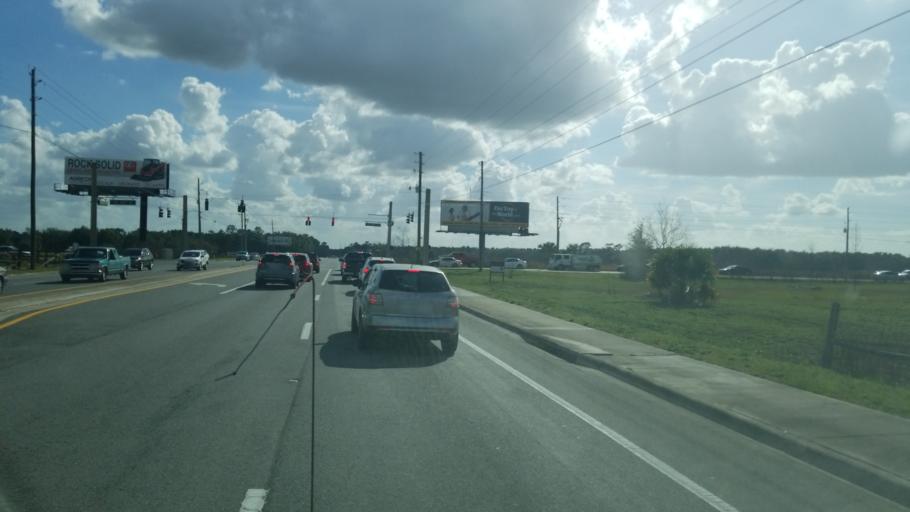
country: US
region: Florida
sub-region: Marion County
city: Ocala
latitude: 29.1509
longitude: -82.2188
